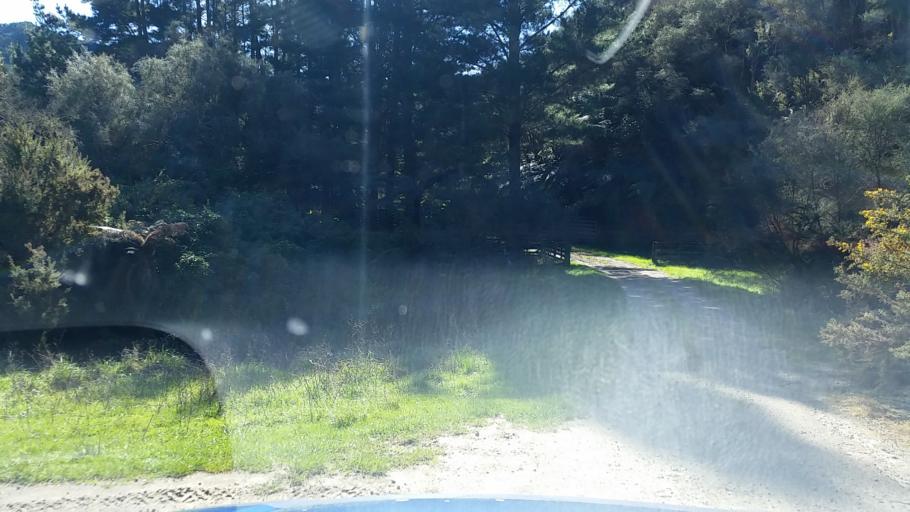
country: NZ
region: Manawatu-Wanganui
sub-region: Wanganui District
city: Wanganui
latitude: -39.6619
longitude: 174.8761
